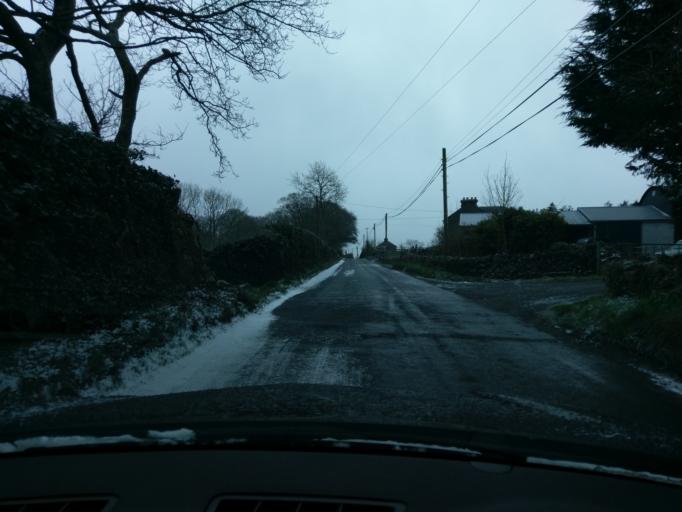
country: IE
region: Connaught
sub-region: County Galway
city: Oranmore
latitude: 53.2407
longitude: -8.8623
